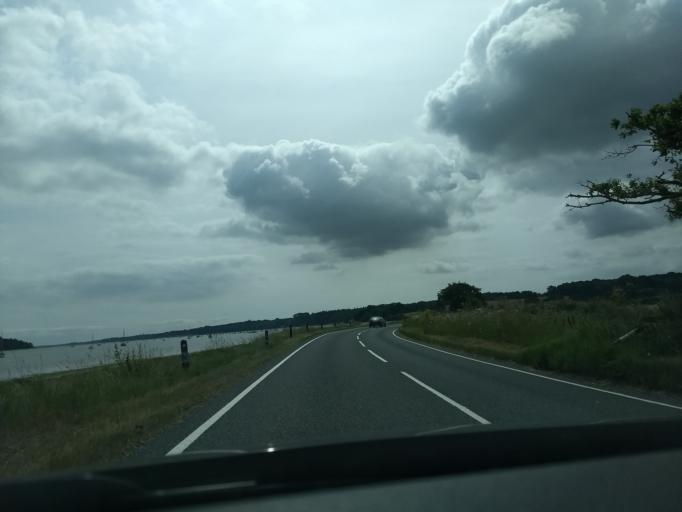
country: GB
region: England
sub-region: Suffolk
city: Ipswich
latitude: 52.0239
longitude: 1.1629
